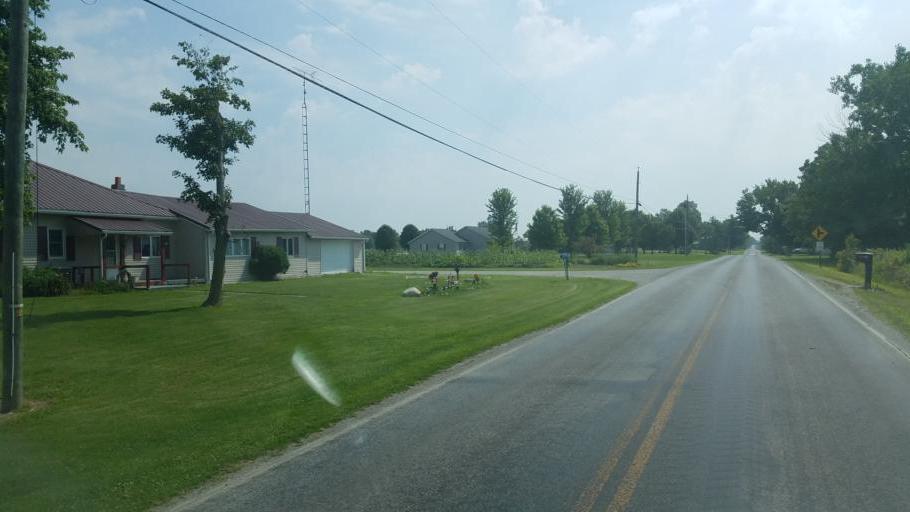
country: US
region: Ohio
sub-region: Hardin County
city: Kenton
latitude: 40.6212
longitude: -83.4731
